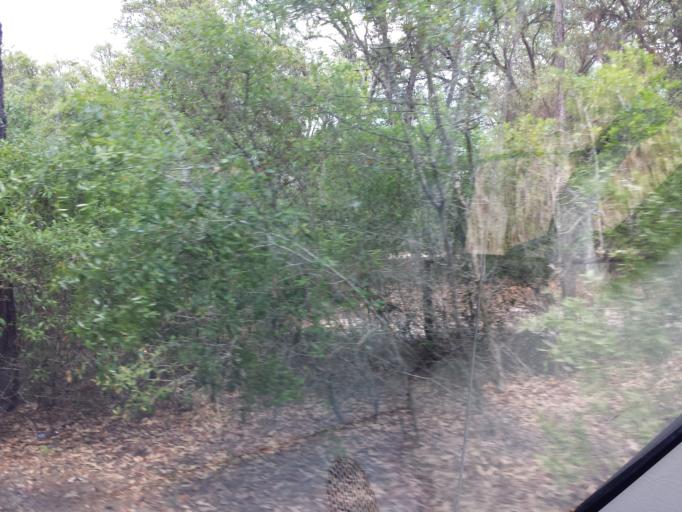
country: US
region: Florida
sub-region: Hernando County
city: Hill 'n Dale
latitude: 28.5329
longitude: -82.2592
